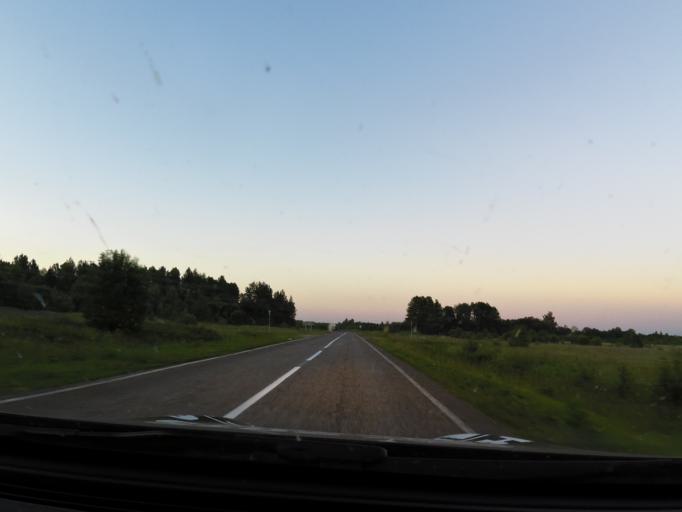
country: RU
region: Kostroma
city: Buy
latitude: 58.3522
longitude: 41.1748
